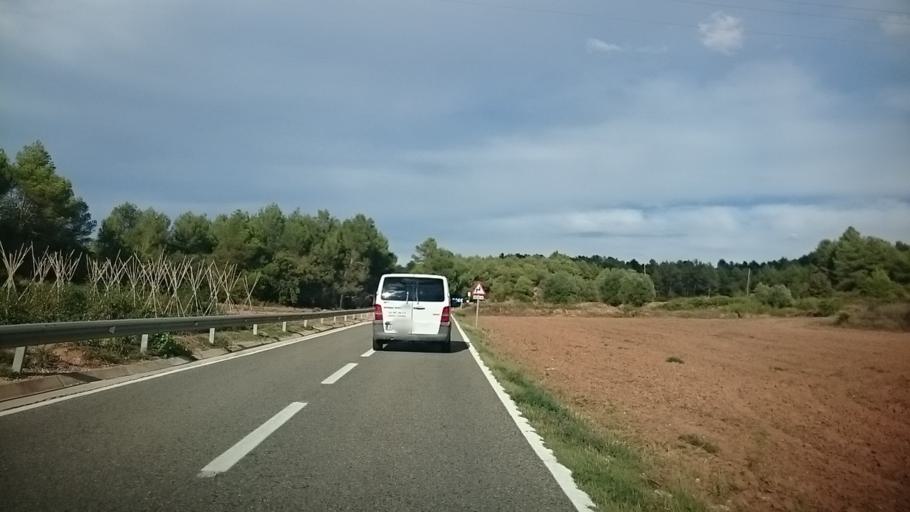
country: ES
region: Catalonia
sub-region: Provincia de Barcelona
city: Odena
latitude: 41.6242
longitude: 1.6586
